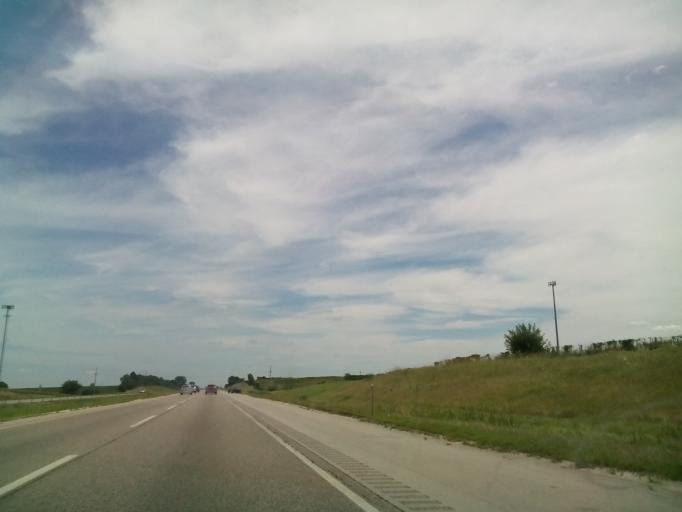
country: US
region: Illinois
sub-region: DeKalb County
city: Cortland
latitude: 41.9008
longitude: -88.6634
